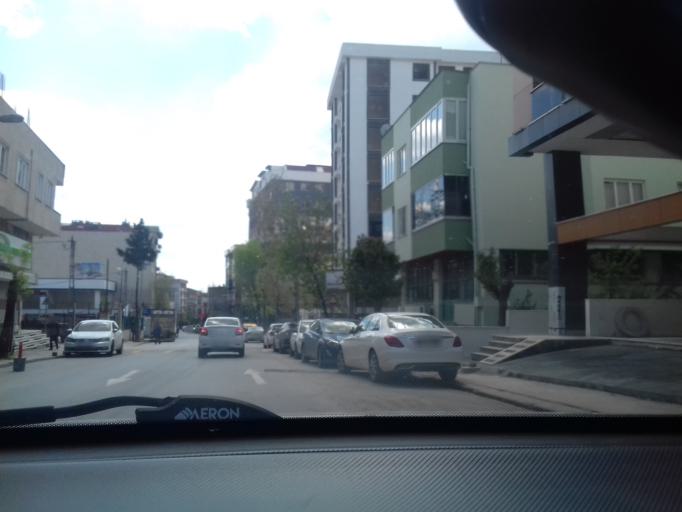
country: TR
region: Istanbul
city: Pendik
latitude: 40.8985
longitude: 29.2732
